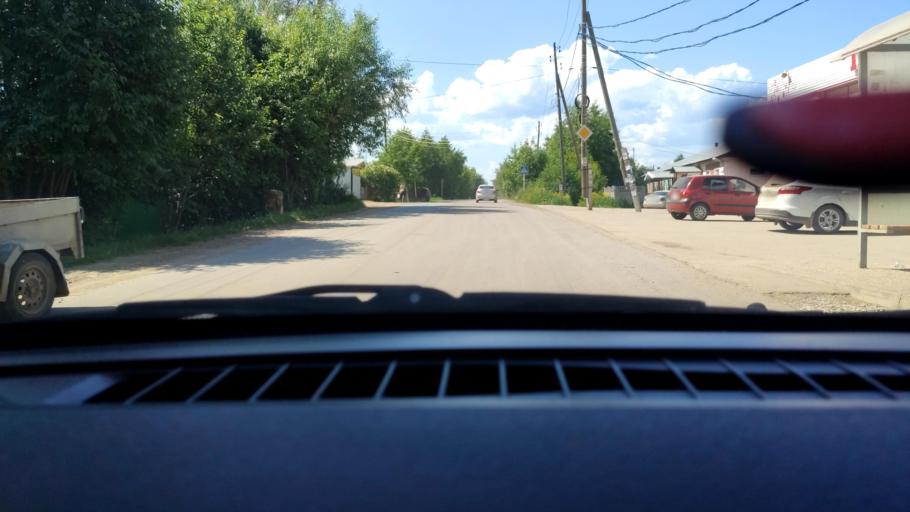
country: RU
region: Perm
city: Sylva
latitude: 58.0325
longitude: 56.7721
